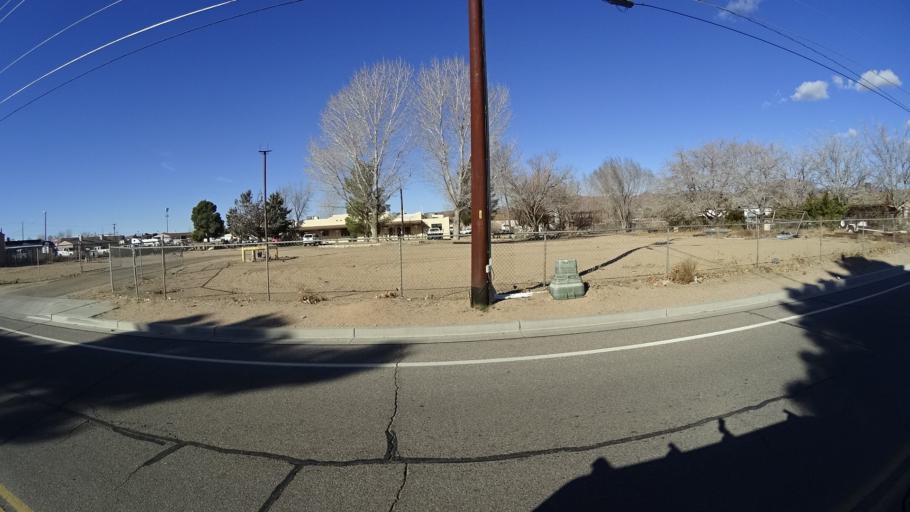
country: US
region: Arizona
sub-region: Mohave County
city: New Kingman-Butler
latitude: 35.2224
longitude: -114.0114
